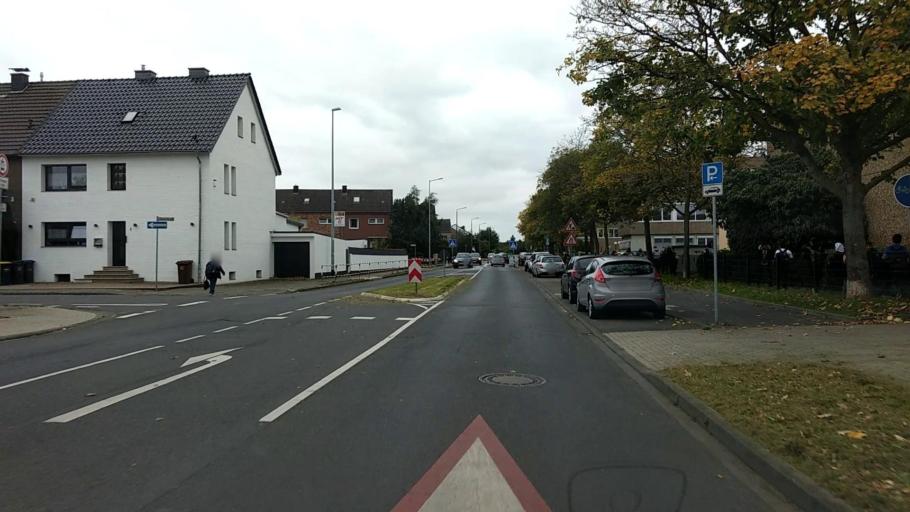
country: DE
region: North Rhine-Westphalia
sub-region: Regierungsbezirk Koln
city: Bergheim
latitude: 50.9499
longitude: 6.6355
